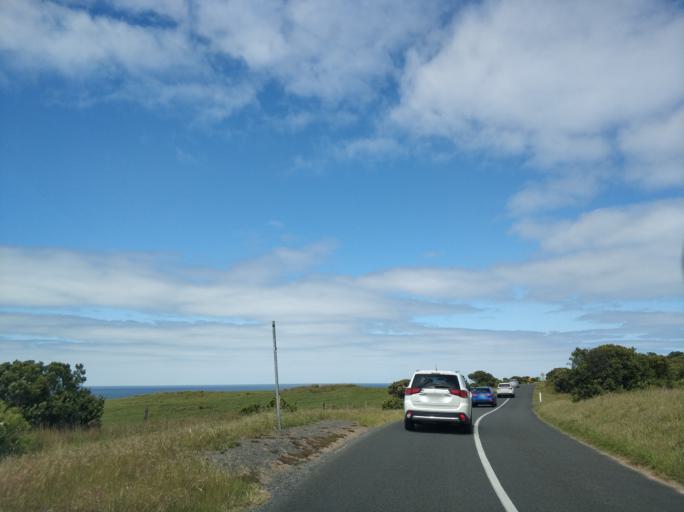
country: AU
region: Victoria
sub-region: Colac-Otway
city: Apollo Bay
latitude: -38.8492
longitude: 143.5364
